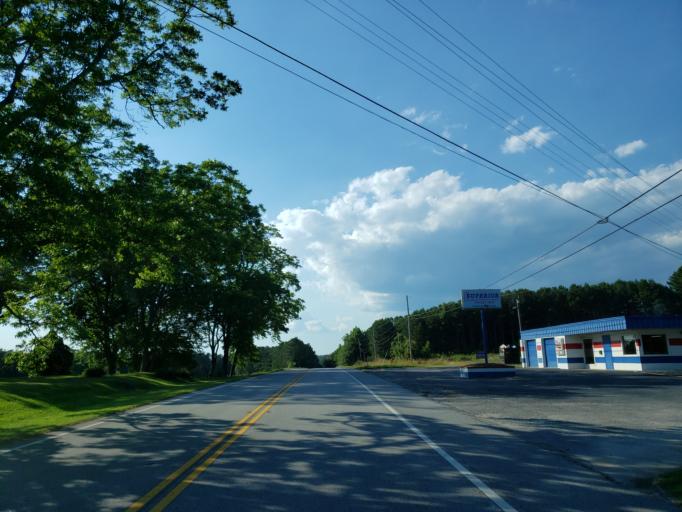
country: US
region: Georgia
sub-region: Haralson County
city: Bremen
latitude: 33.7451
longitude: -85.1546
